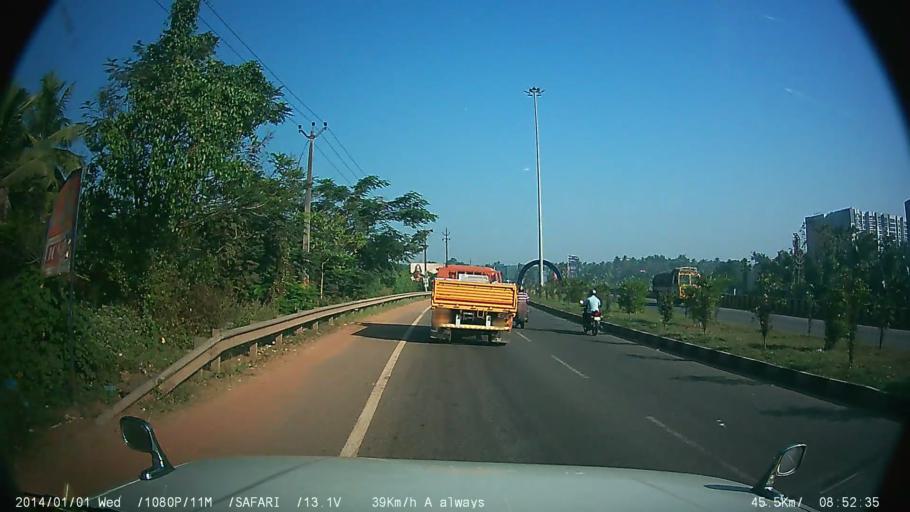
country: IN
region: Kerala
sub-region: Ernakulam
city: Angamali
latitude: 10.2067
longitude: 76.3819
